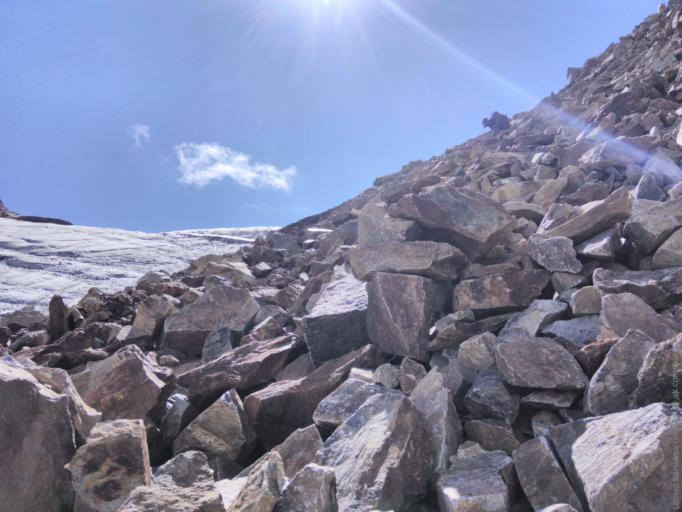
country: RU
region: Kabardino-Balkariya
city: Terskol
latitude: 43.2626
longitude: 42.4144
